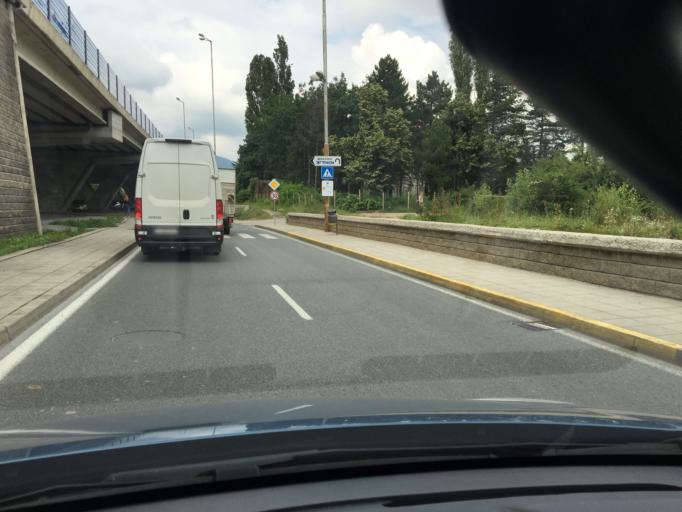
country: BG
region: Sofia-Capital
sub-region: Stolichna Obshtina
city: Sofia
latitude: 42.6241
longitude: 23.3619
